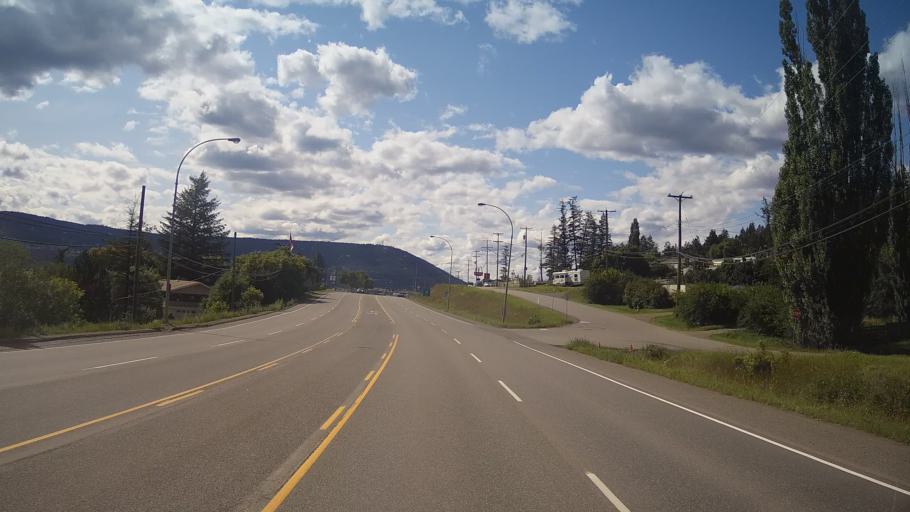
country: CA
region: British Columbia
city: Williams Lake
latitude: 52.1234
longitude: -122.1136
